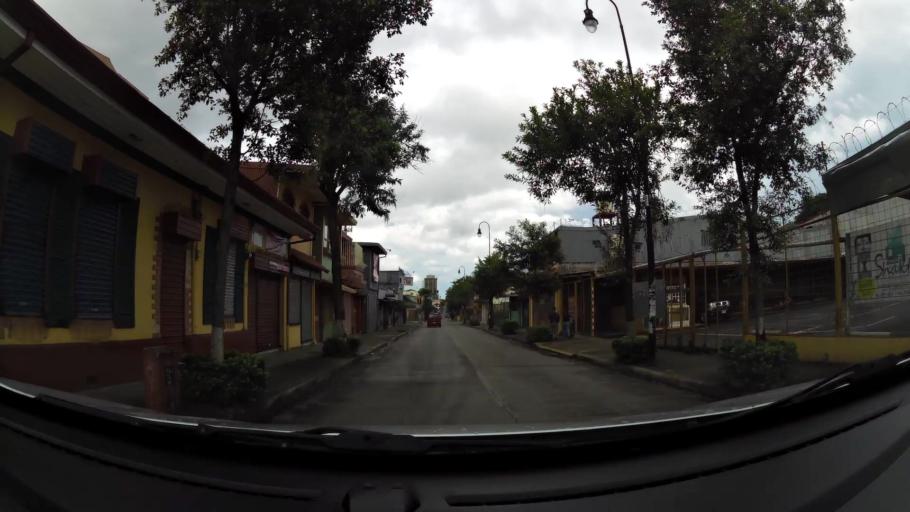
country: CR
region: San Jose
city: San Jose
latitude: 9.9302
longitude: -84.0732
